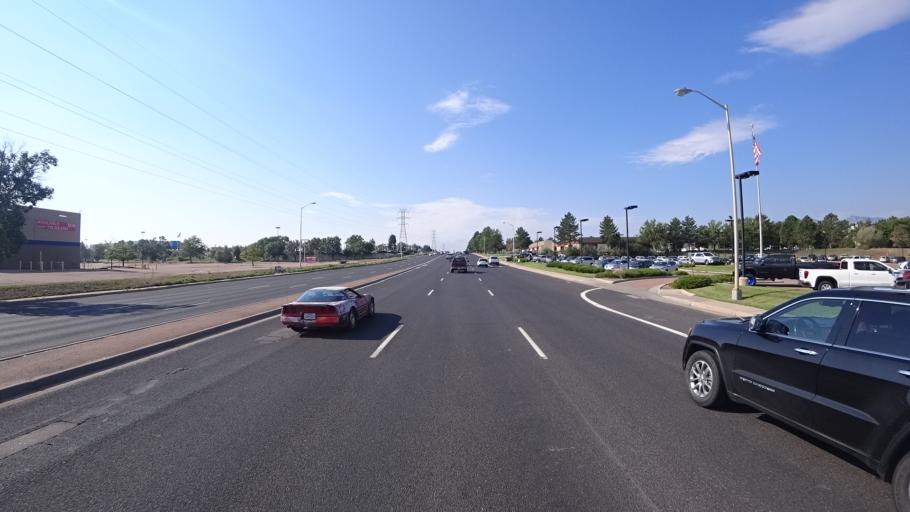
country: US
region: Colorado
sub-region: El Paso County
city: Stratmoor
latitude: 38.8196
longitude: -104.7576
